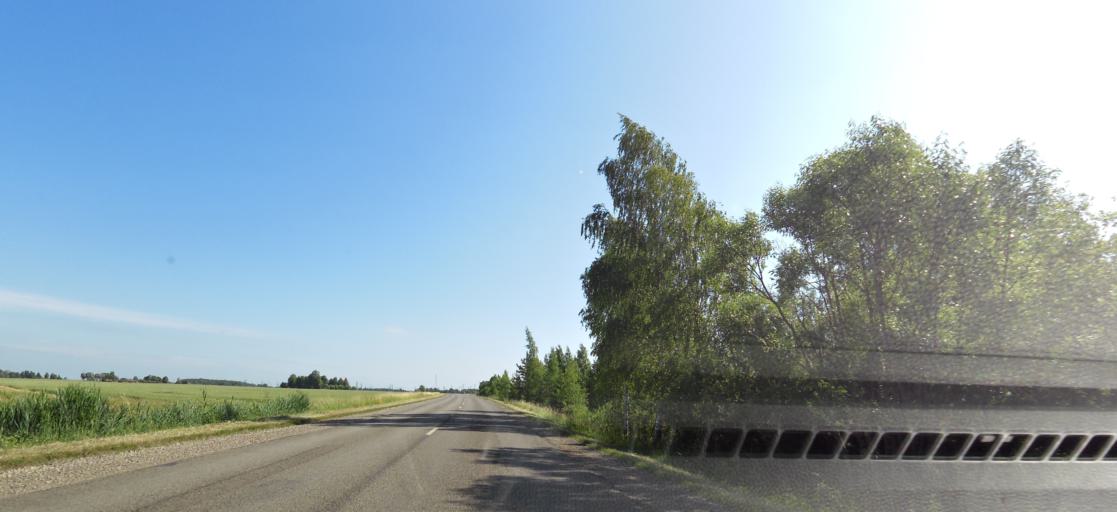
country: LT
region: Panevezys
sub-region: Birzai
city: Birzai
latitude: 56.2256
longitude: 24.8083
